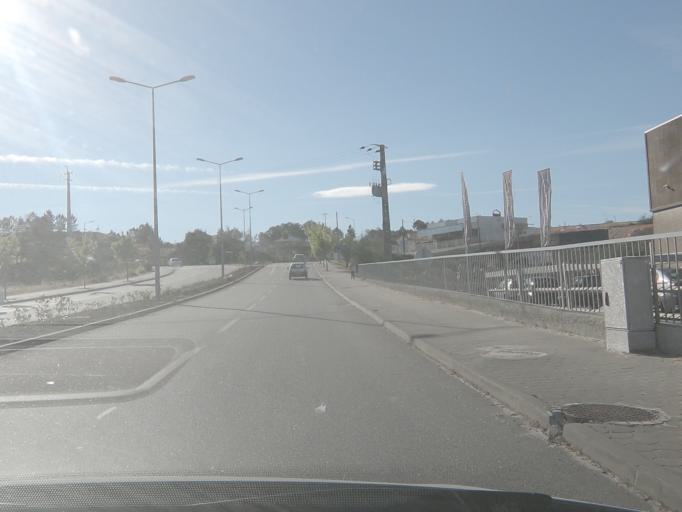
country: PT
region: Viseu
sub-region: Viseu
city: Abraveses
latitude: 40.6926
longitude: -7.9289
